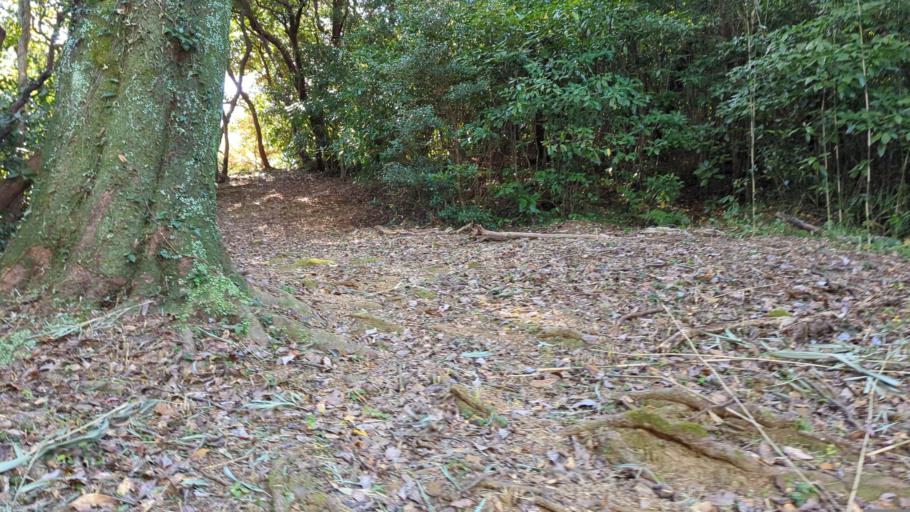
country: JP
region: Shizuoka
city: Kosai-shi
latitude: 34.7815
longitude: 137.4823
